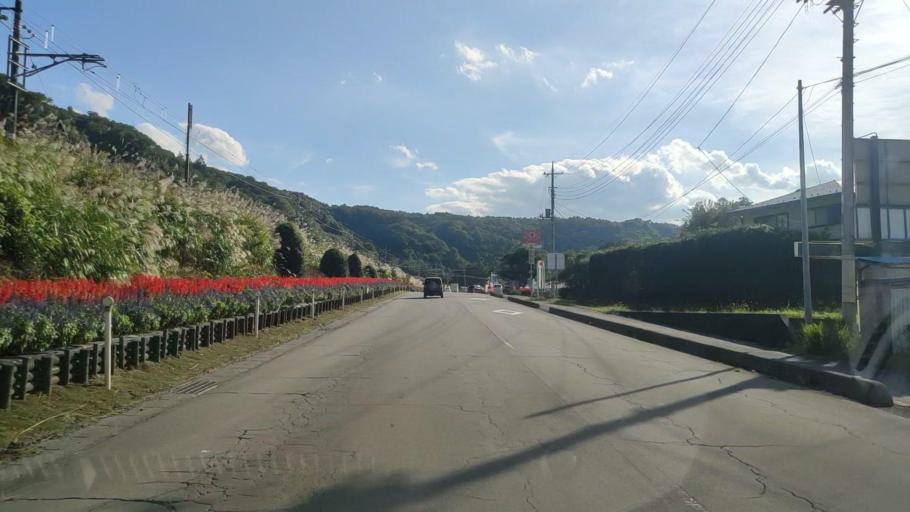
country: JP
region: Nagano
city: Komoro
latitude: 36.5229
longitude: 138.5423
